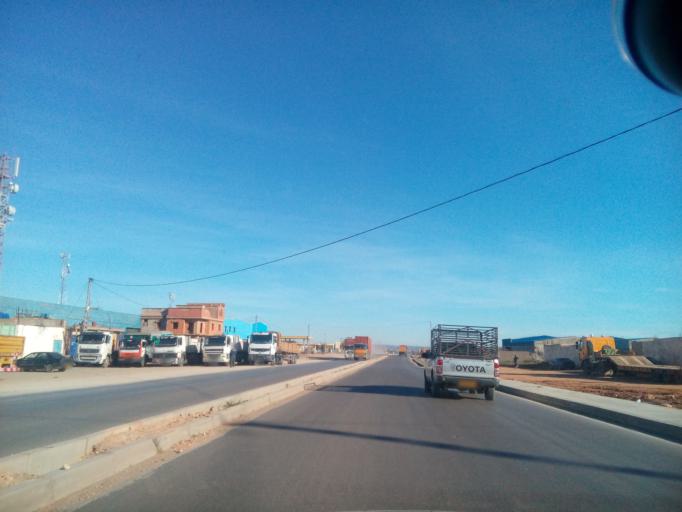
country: DZ
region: Mostaganem
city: Mostaganem
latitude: 35.9117
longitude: 0.1475
